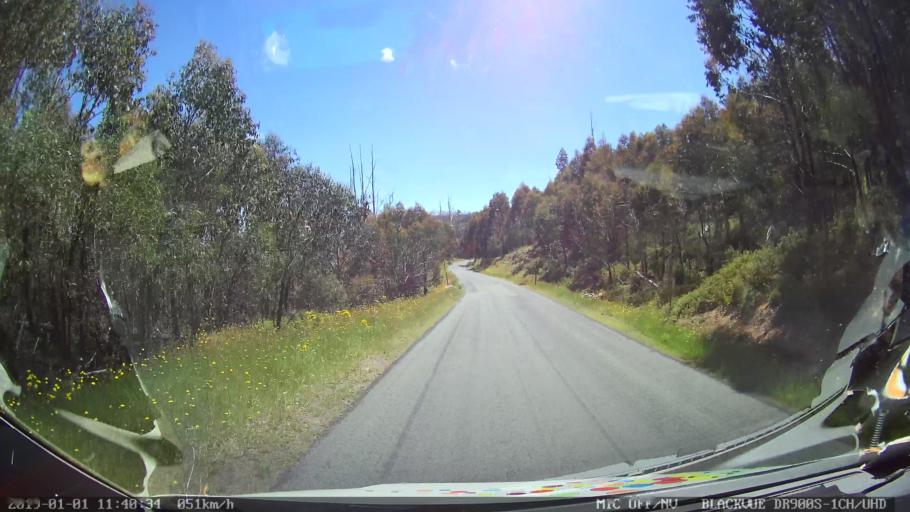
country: AU
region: New South Wales
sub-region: Snowy River
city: Jindabyne
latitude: -35.9193
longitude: 148.3871
